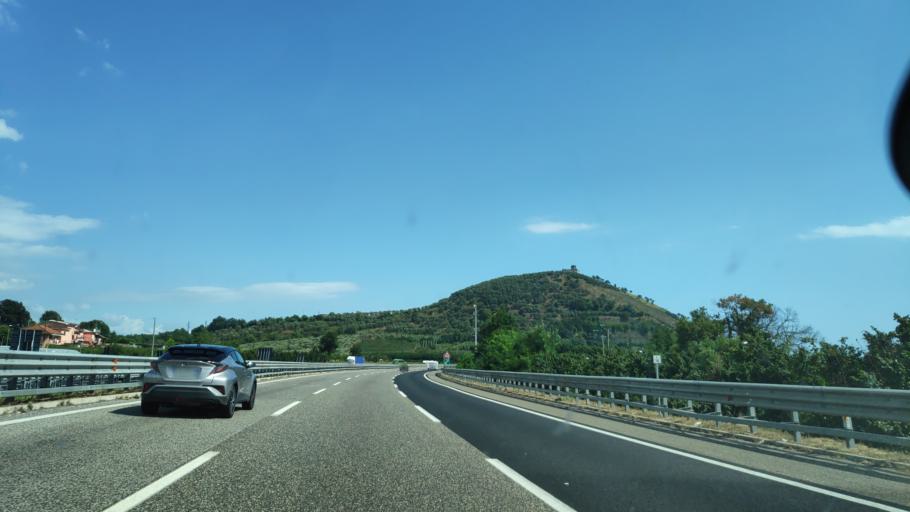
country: IT
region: Campania
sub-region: Provincia di Salerno
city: Pezzano-Filetta
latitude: 40.6839
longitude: 14.8544
